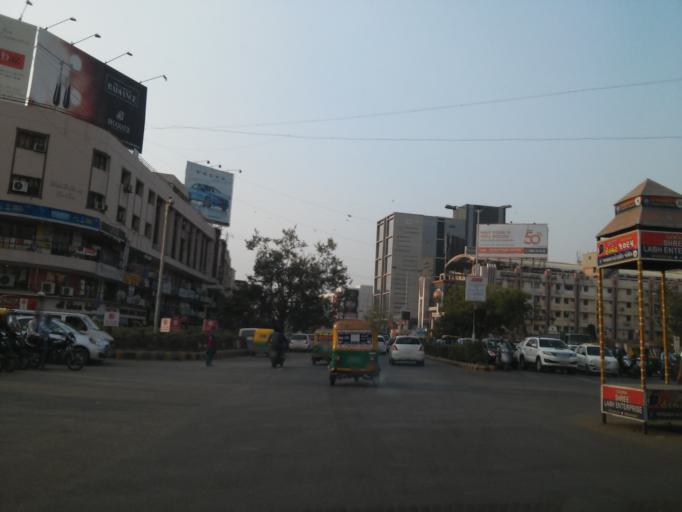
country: IN
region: Gujarat
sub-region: Ahmadabad
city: Sarkhej
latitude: 23.0320
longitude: 72.5252
